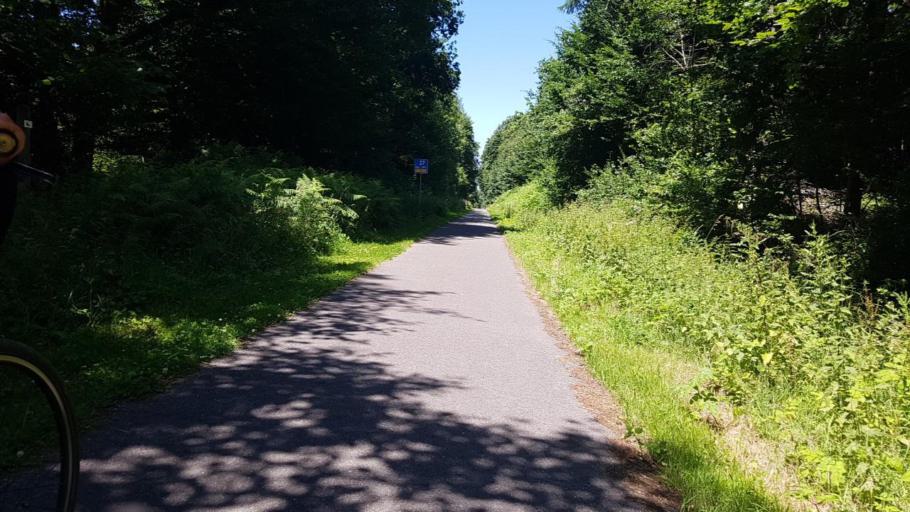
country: BE
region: Wallonia
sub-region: Province du Hainaut
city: Froidchapelle
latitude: 50.1601
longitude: 4.2530
